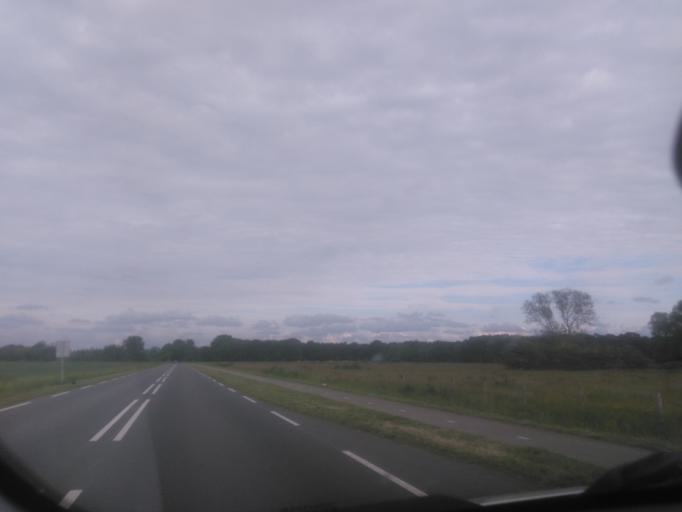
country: NL
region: Zeeland
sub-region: Gemeente Hulst
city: Hulst
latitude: 51.2740
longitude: 4.0971
